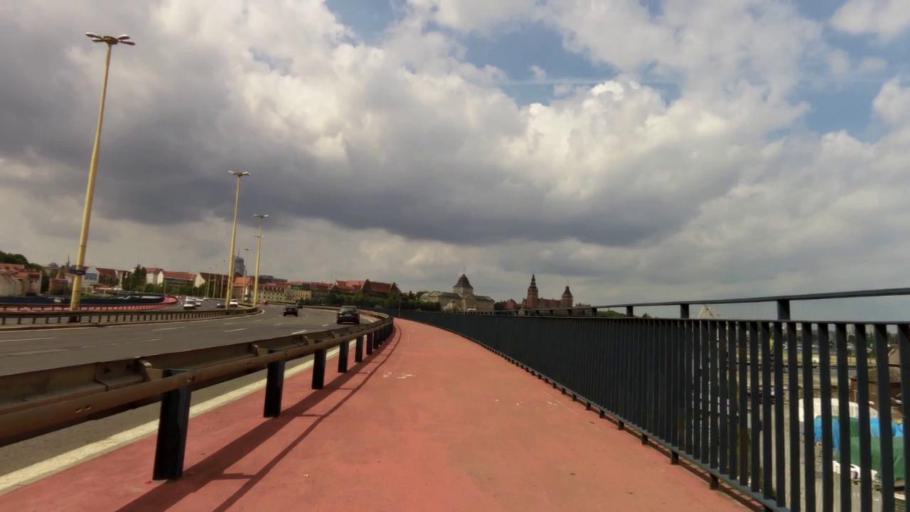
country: PL
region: West Pomeranian Voivodeship
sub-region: Szczecin
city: Szczecin
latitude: 53.4242
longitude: 14.5679
